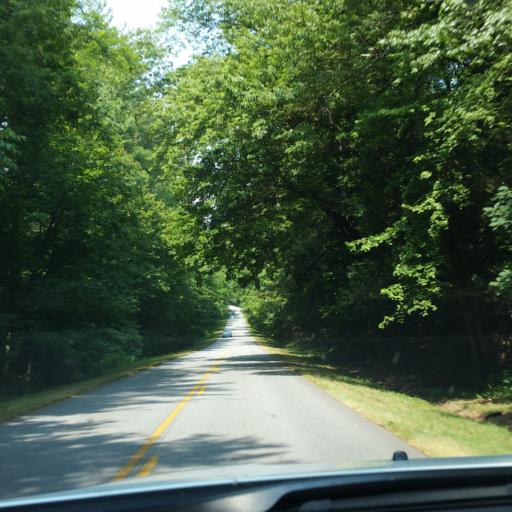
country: US
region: North Carolina
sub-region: Buncombe County
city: Biltmore Forest
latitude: 35.5157
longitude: -82.5341
